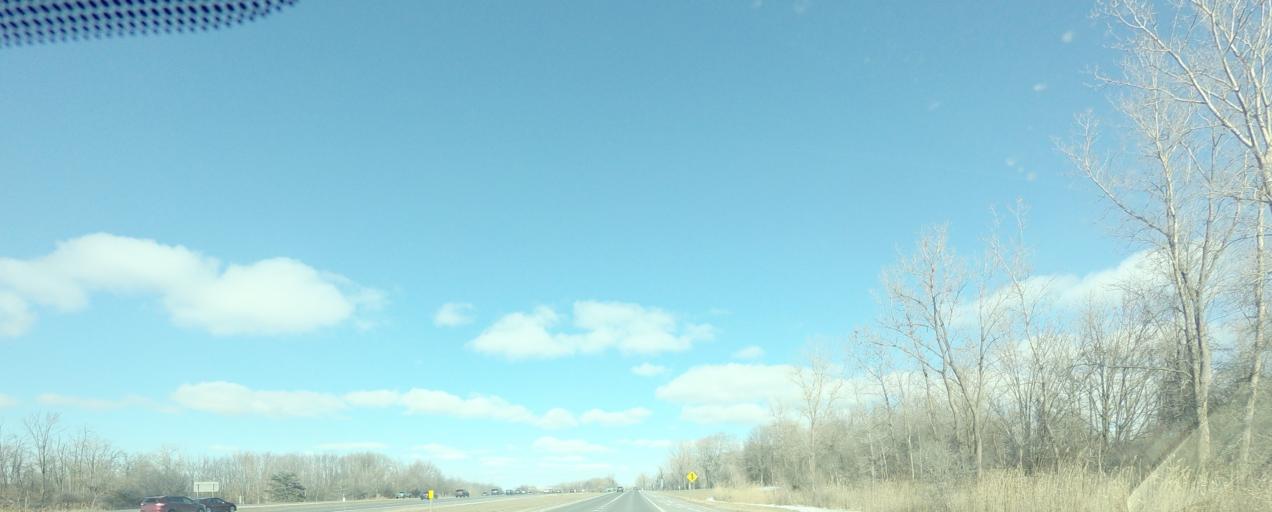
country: US
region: New York
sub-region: Onondaga County
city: North Syracuse
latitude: 43.1160
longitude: -76.1351
